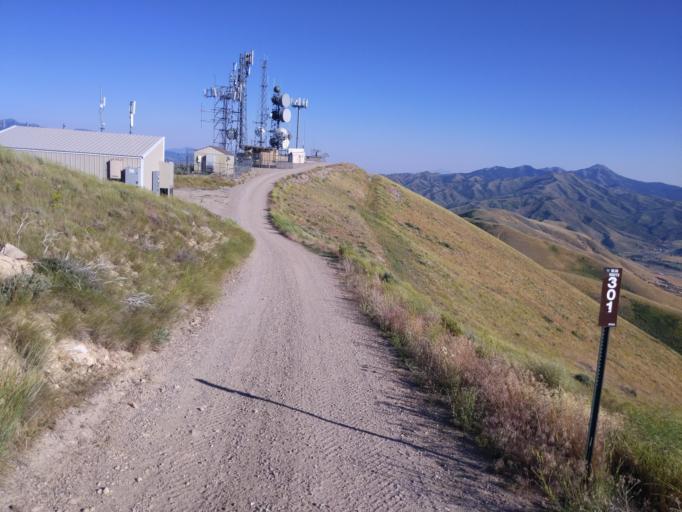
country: US
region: Idaho
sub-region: Bannock County
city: Pocatello
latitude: 42.8484
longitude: -112.3625
